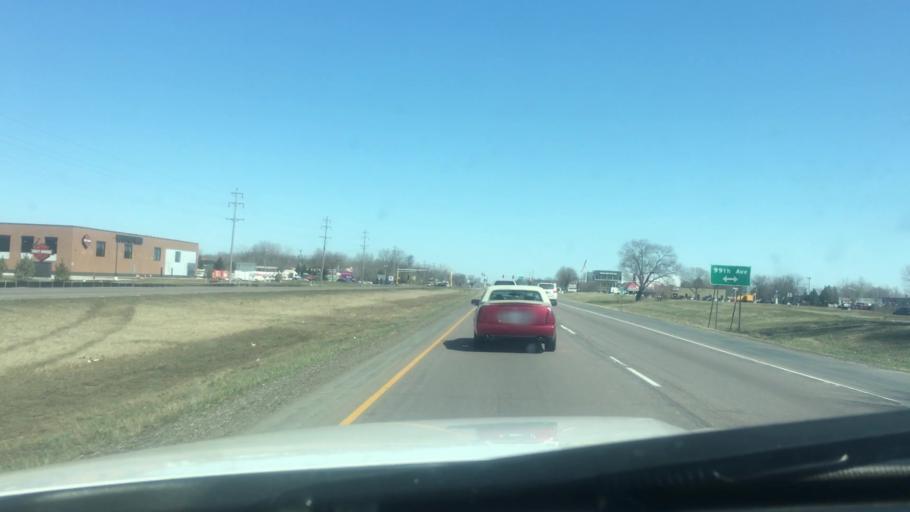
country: US
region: Minnesota
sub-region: Anoka County
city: Blaine
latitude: 45.1468
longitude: -93.2352
